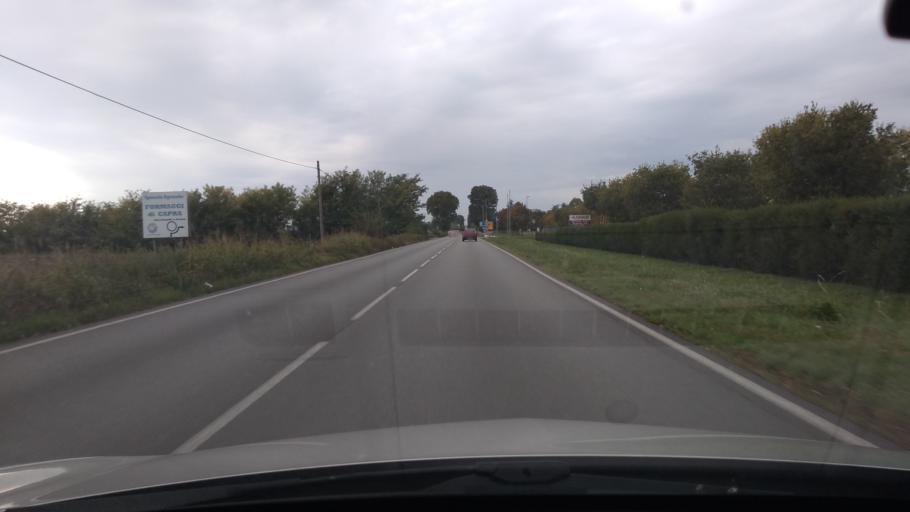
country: IT
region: Lombardy
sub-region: Provincia di Bergamo
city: Cologno al Serio
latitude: 45.5885
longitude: 9.7201
